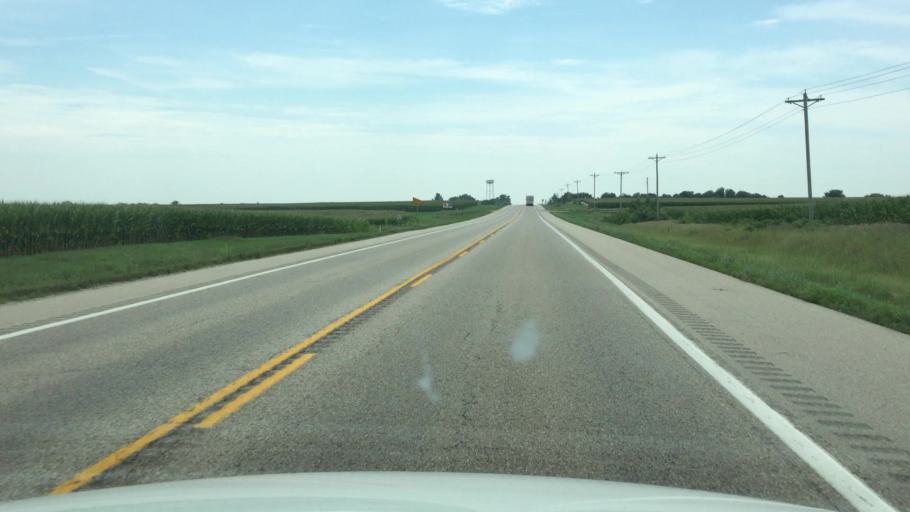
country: US
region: Kansas
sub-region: Nemaha County
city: Sabetha
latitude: 39.7132
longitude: -95.7300
